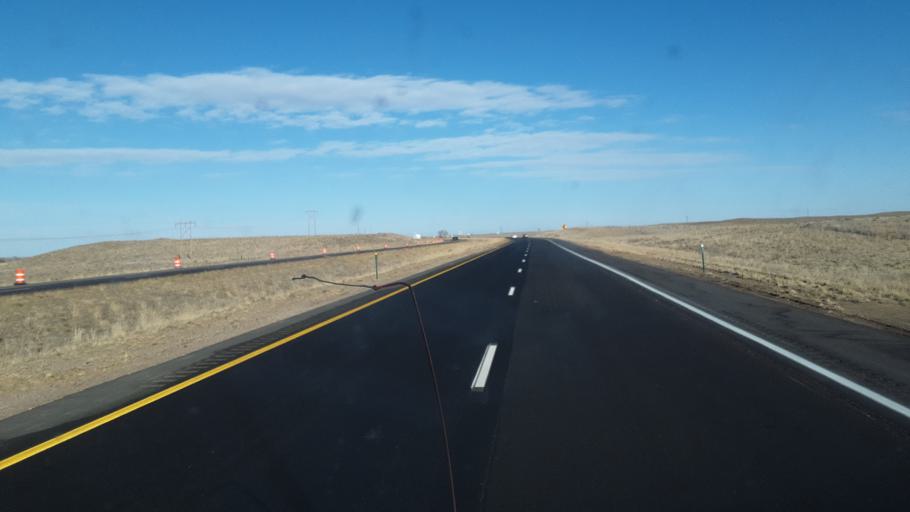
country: US
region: Colorado
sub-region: Morgan County
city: Brush
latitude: 40.2740
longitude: -103.5761
